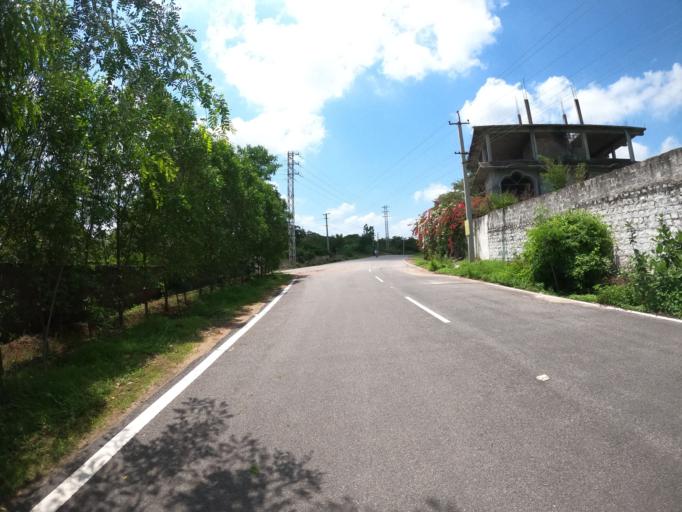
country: IN
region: Telangana
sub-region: Medak
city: Serilingampalle
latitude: 17.3715
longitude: 78.3236
